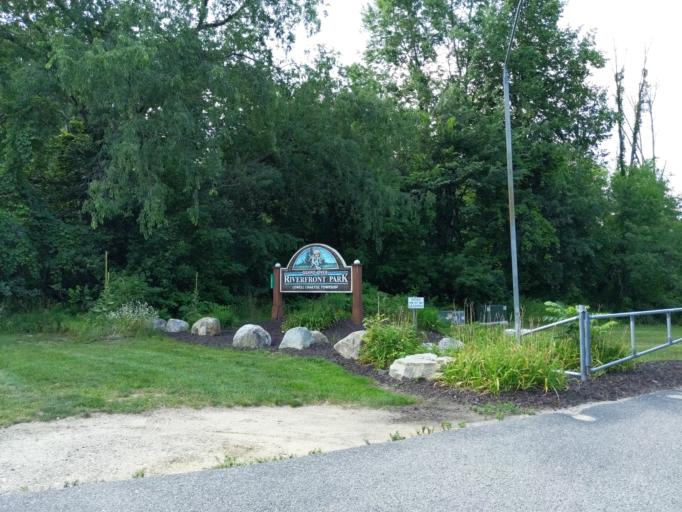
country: US
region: Michigan
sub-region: Kent County
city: Lowell
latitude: 42.9222
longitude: -85.3691
